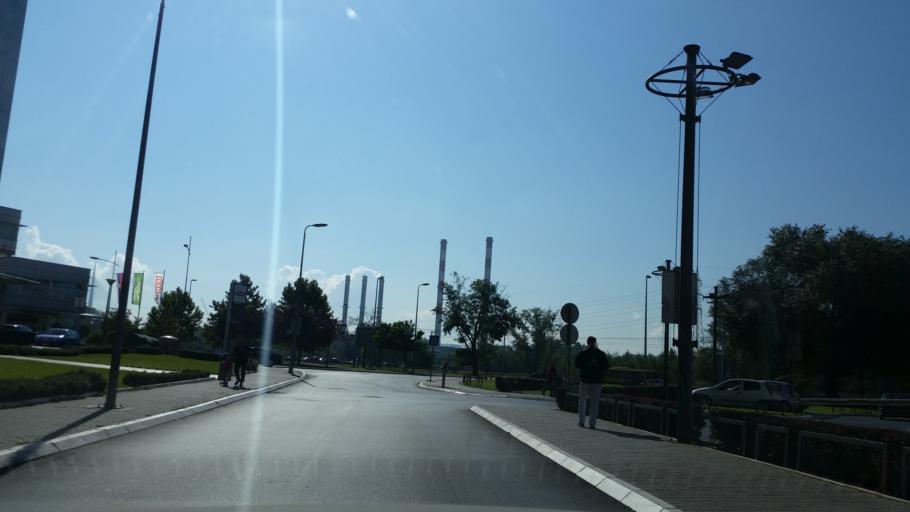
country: RS
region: Central Serbia
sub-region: Belgrade
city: Novi Beograd
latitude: 44.8052
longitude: 20.4068
